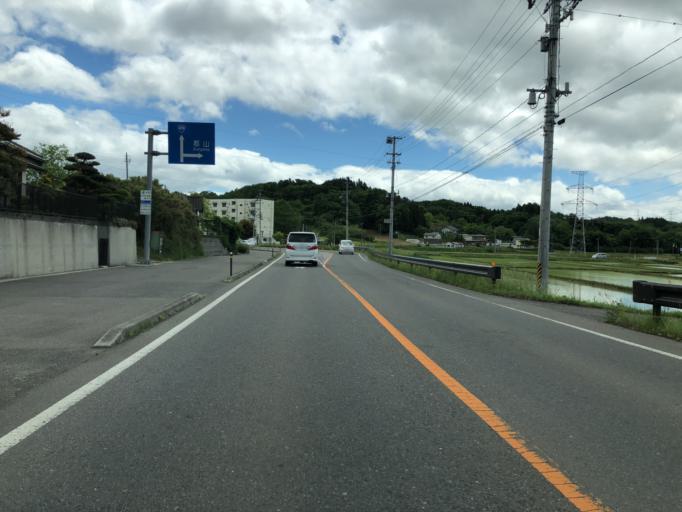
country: JP
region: Fukushima
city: Motomiya
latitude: 37.5080
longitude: 140.4329
